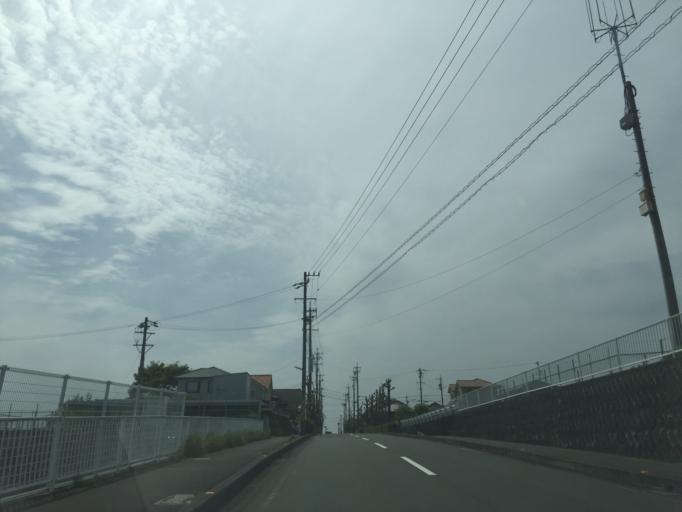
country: JP
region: Shizuoka
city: Kakegawa
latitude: 34.7810
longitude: 138.0257
